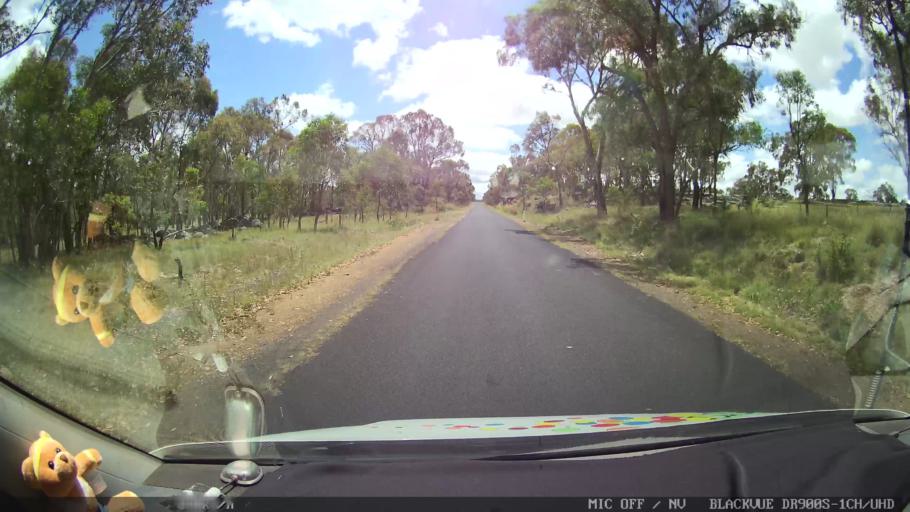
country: AU
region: New South Wales
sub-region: Glen Innes Severn
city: Glen Innes
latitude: -29.4318
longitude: 151.6882
